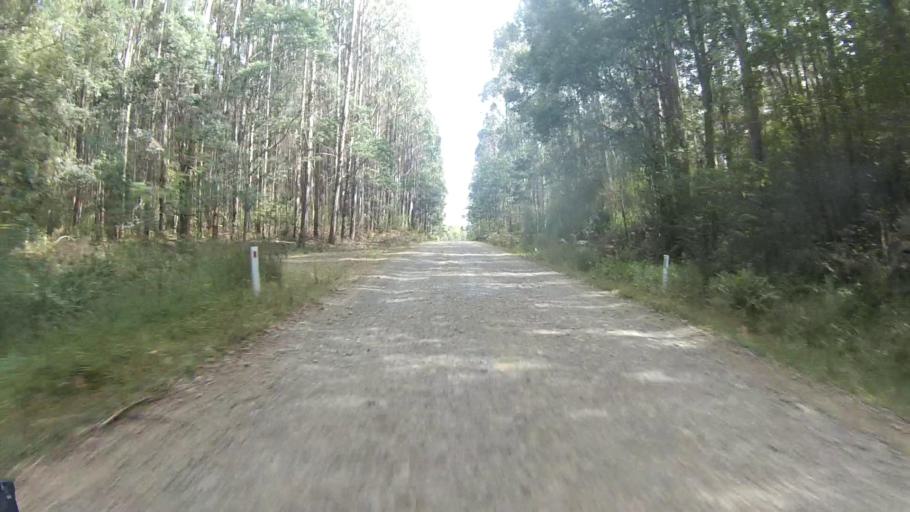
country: AU
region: Tasmania
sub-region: Sorell
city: Sorell
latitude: -42.7456
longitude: 147.8288
